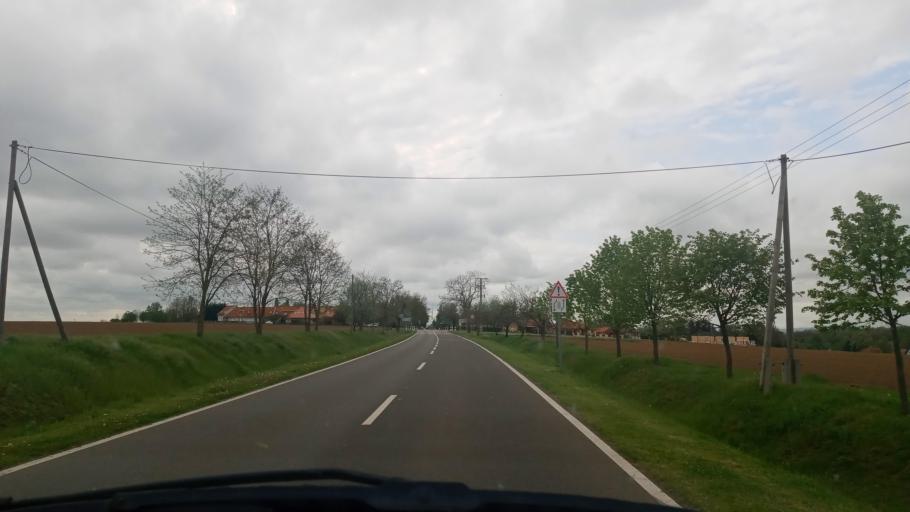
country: HU
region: Baranya
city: Kozarmisleny
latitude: 46.0083
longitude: 18.3742
